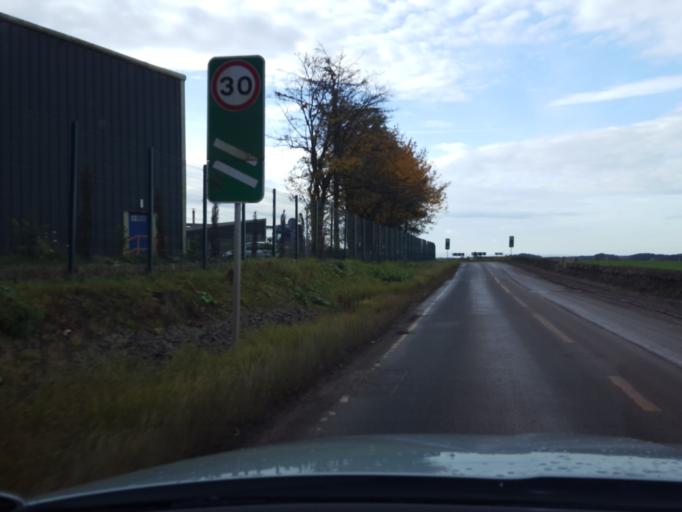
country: GB
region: Scotland
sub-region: South Lanarkshire
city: Carnwath
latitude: 55.7056
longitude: -3.6145
